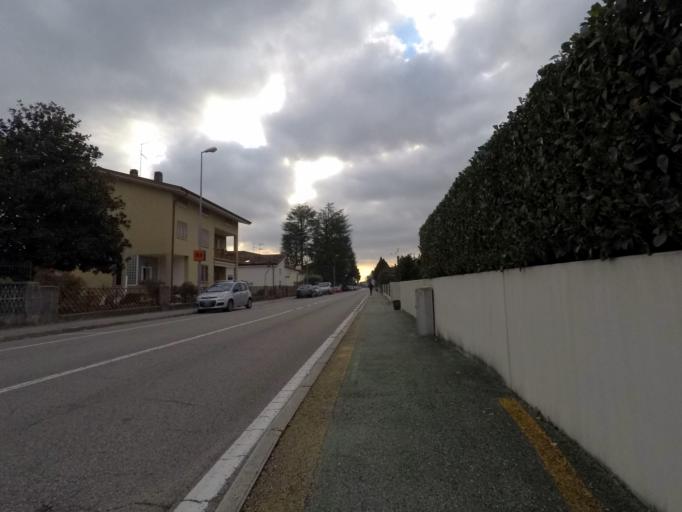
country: IT
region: Friuli Venezia Giulia
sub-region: Provincia di Udine
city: Tavagnacco
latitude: 46.1072
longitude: 13.2144
